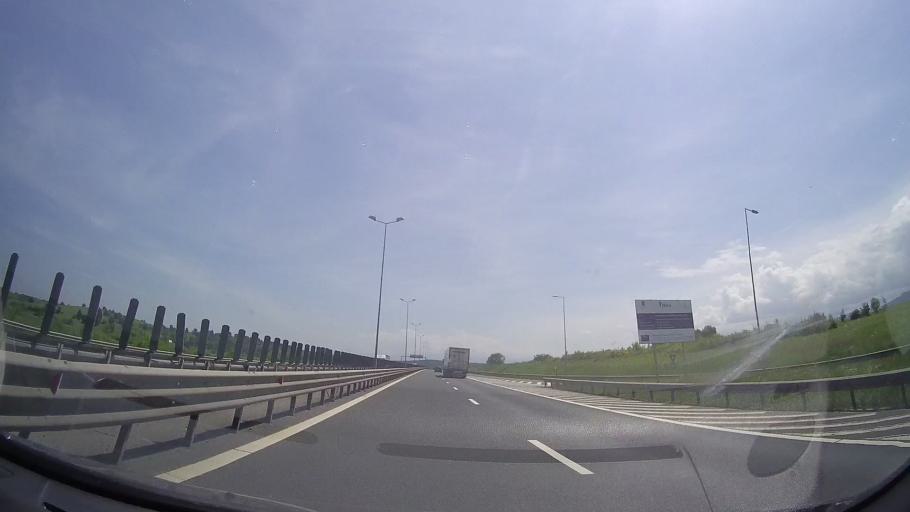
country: RO
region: Sibiu
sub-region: Oras Saliste
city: Saliste
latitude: 45.8073
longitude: 23.9079
